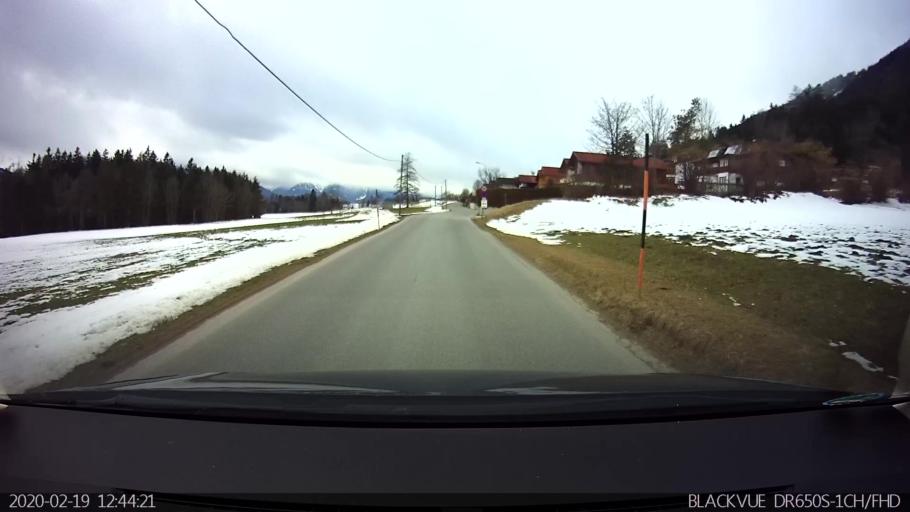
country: AT
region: Tyrol
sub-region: Politischer Bezirk Innsbruck Land
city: Fritzens
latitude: 47.3258
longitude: 11.6016
